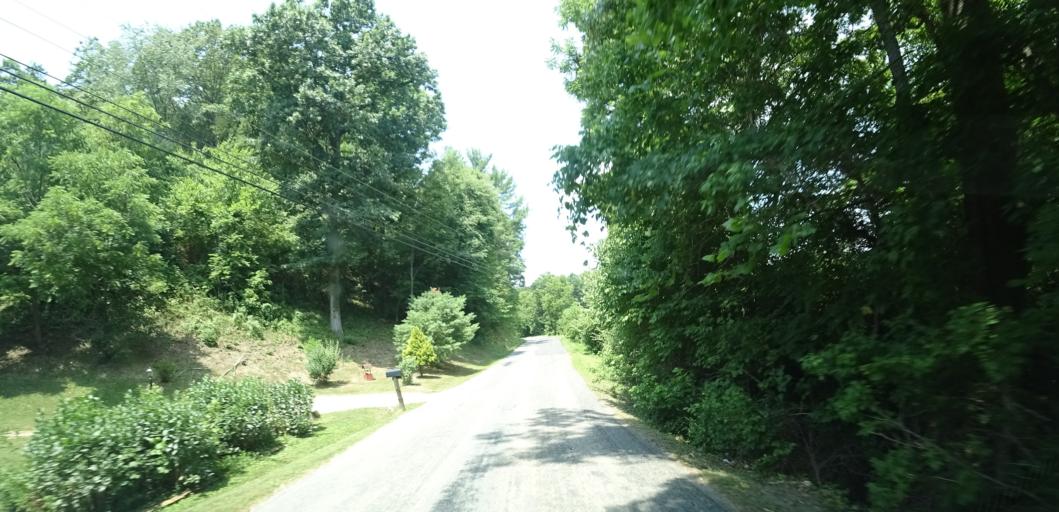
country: US
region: Virginia
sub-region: Botetourt County
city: Fincastle
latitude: 37.4970
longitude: -79.8594
